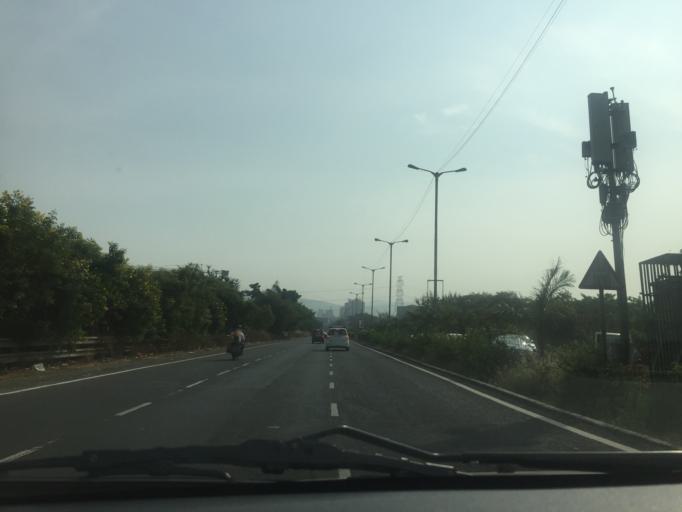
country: IN
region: Maharashtra
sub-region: Thane
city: Airoli
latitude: 19.1501
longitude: 72.9850
